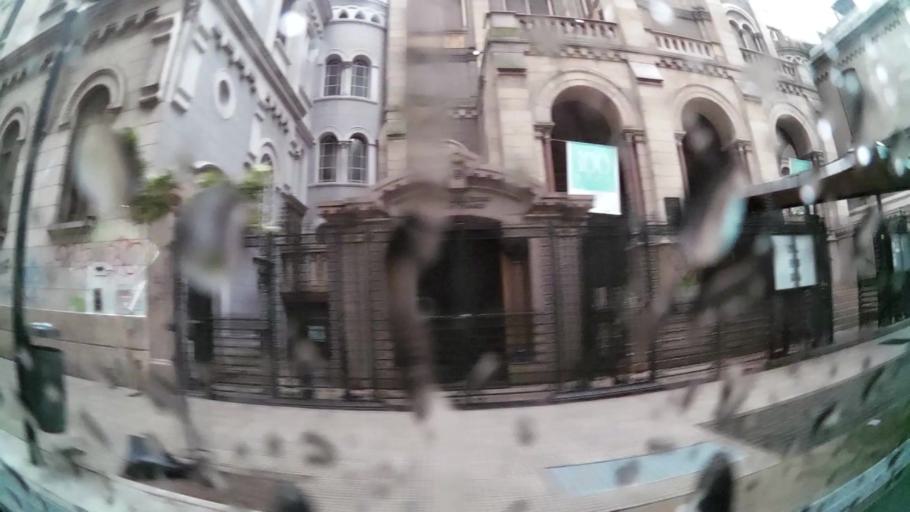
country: AR
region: Buenos Aires F.D.
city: Retiro
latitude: -34.5958
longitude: -58.3745
